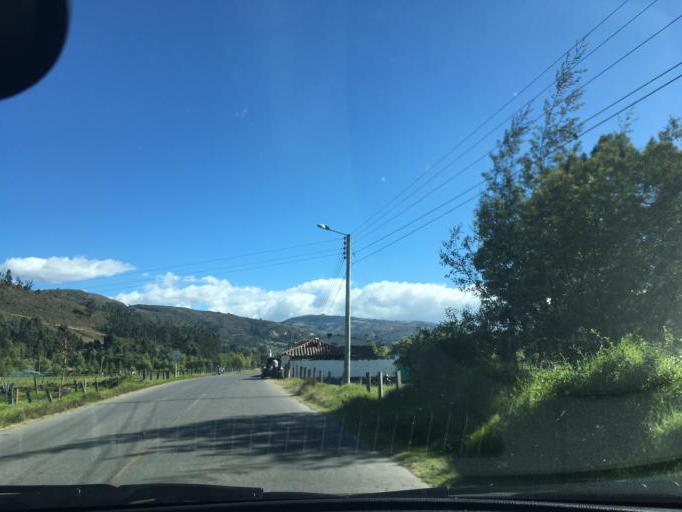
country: CO
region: Boyaca
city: Firavitoba
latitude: 5.6237
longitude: -72.9827
